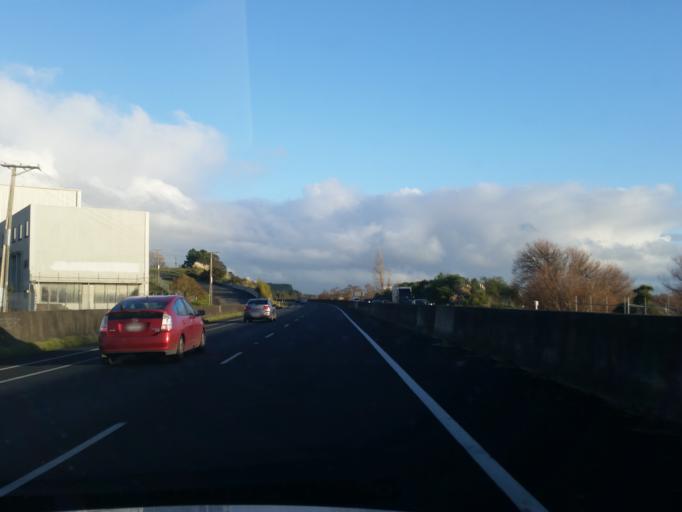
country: NZ
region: Waikato
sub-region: Waikato District
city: Te Kauwhata
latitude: -37.3125
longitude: 175.0669
